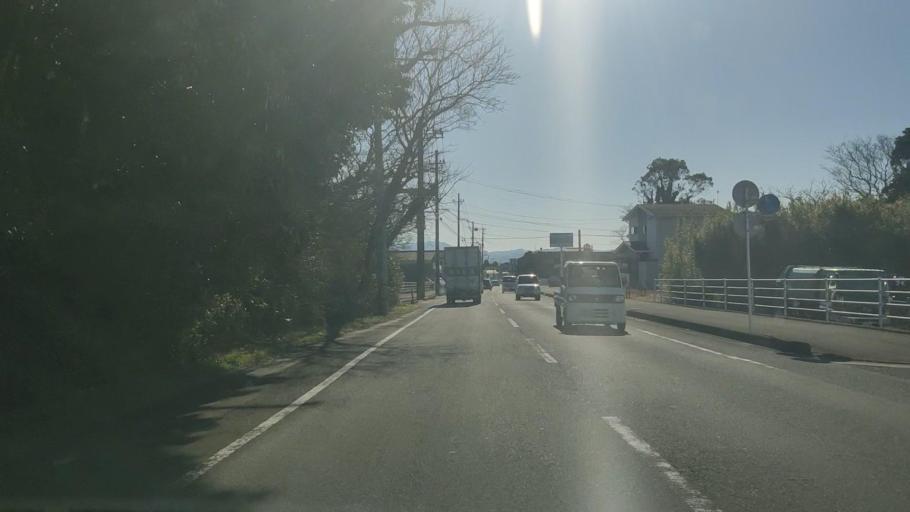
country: JP
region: Miyazaki
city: Miyazaki-shi
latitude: 31.9443
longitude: 131.4582
